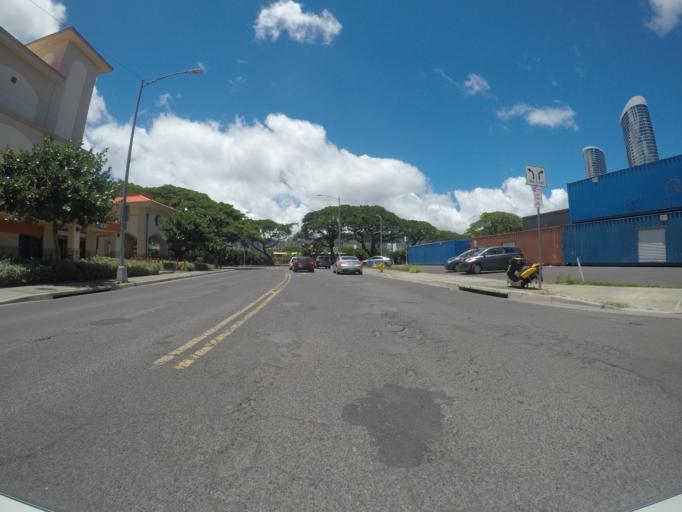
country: US
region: Hawaii
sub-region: Honolulu County
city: Honolulu
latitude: 21.2959
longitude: -157.8501
